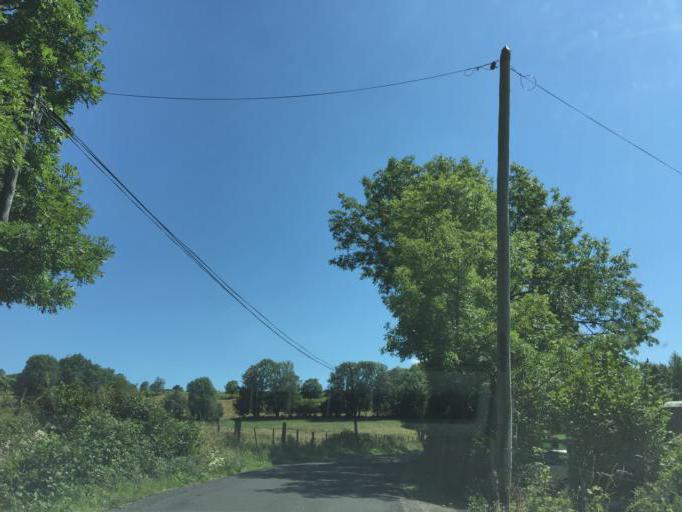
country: FR
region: Midi-Pyrenees
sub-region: Departement de l'Aveyron
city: Laguiole
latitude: 44.6504
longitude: 2.8733
